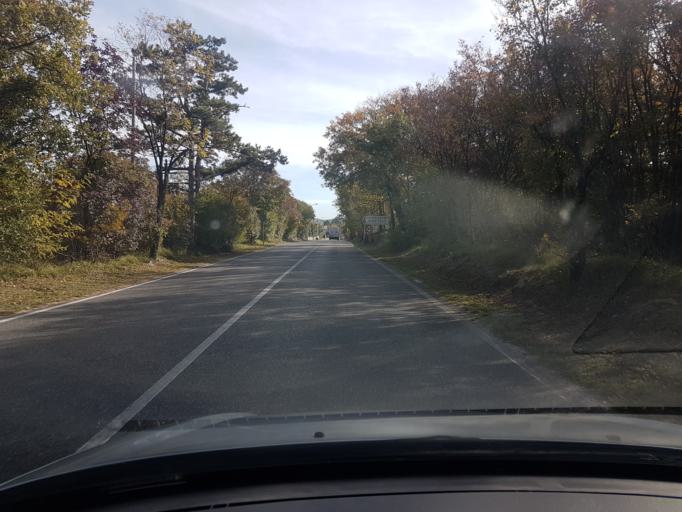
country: IT
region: Friuli Venezia Giulia
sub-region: Provincia di Trieste
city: Prosecco-Contovello
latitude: 45.7219
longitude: 13.7185
